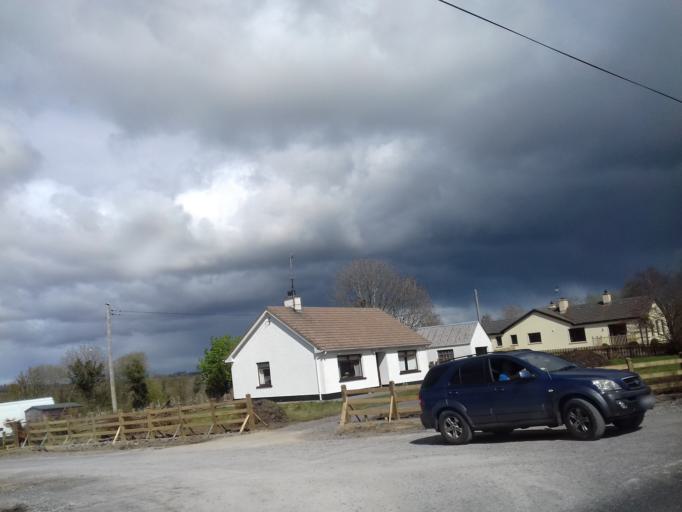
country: IE
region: Ulster
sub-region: County Donegal
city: Ballyshannon
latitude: 54.4678
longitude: -8.0464
